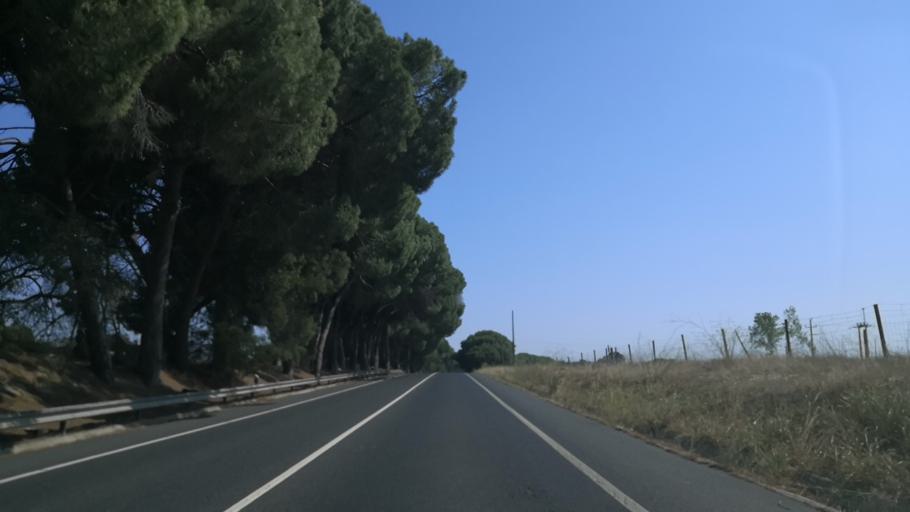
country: PT
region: Evora
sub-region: Vendas Novas
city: Vendas Novas
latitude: 38.7050
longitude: -8.6132
